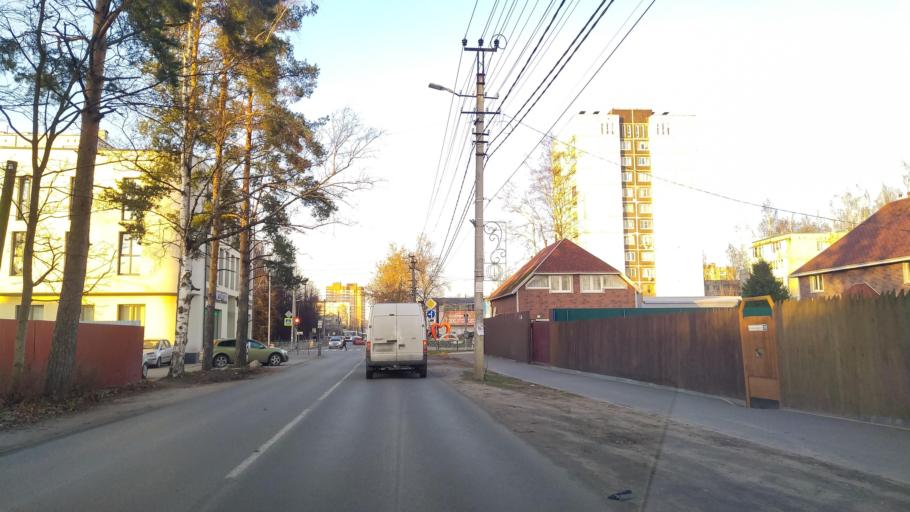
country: RU
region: Leningrad
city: Vsevolozhsk
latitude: 60.0226
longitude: 30.6320
